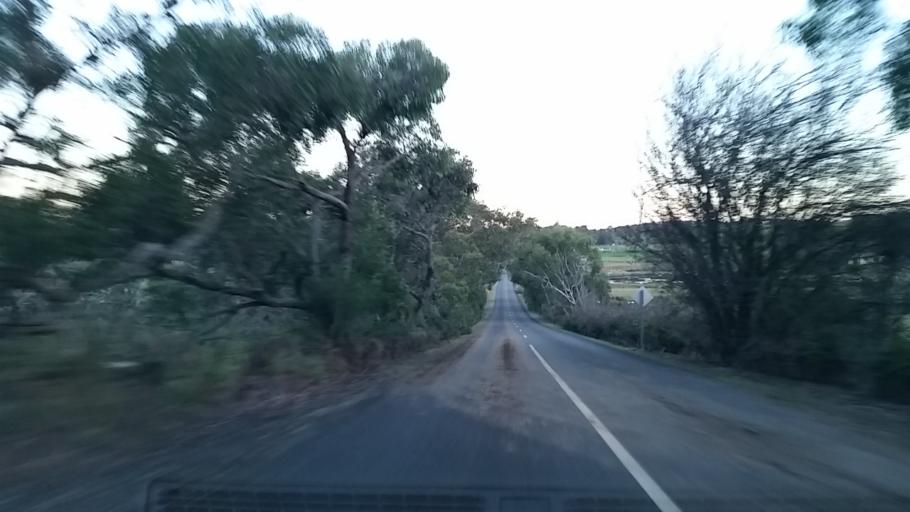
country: AU
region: South Australia
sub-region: Alexandrina
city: Mount Compass
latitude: -35.3109
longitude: 138.6178
